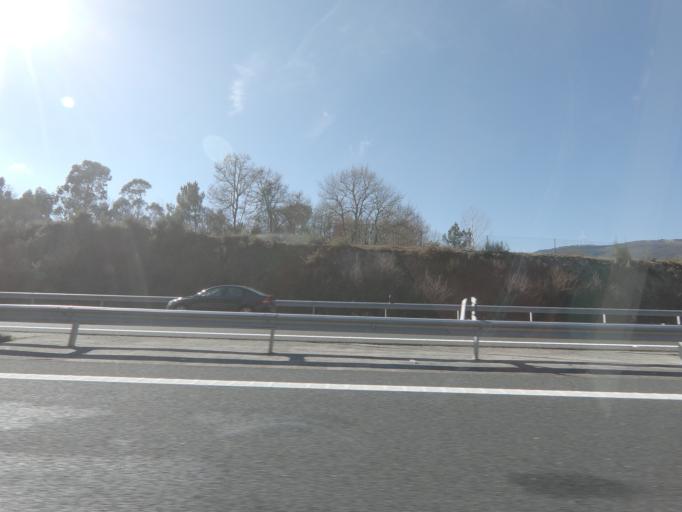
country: ES
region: Galicia
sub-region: Provincia de Ourense
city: Pinor
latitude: 42.4910
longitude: -8.0243
